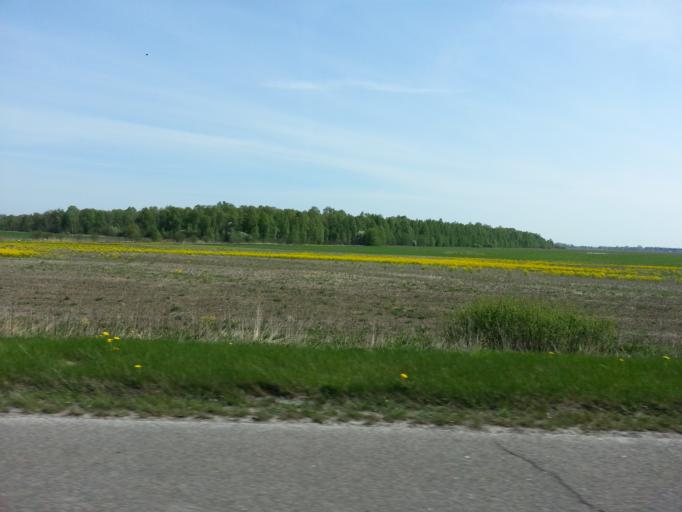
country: LT
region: Panevezys
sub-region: Panevezys City
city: Panevezys
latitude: 55.6039
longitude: 24.4379
